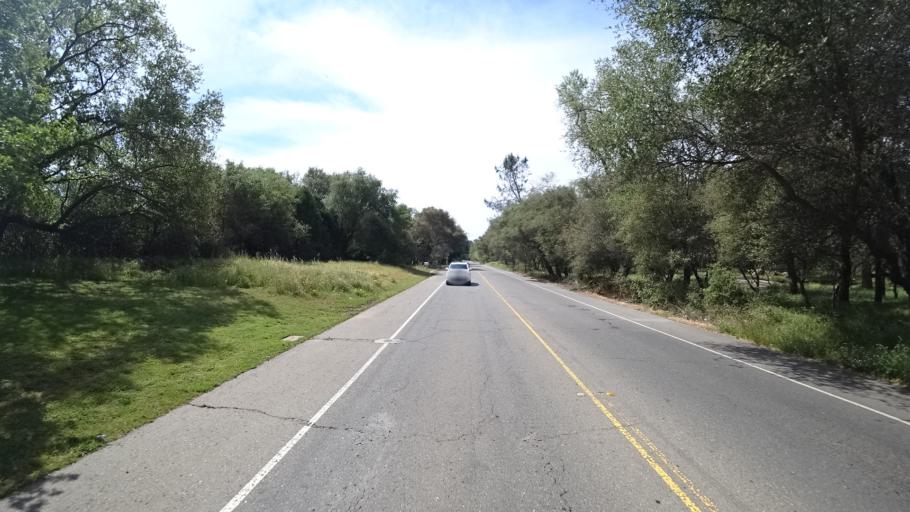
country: US
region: California
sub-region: Placer County
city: Loomis
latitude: 38.8237
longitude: -121.2174
